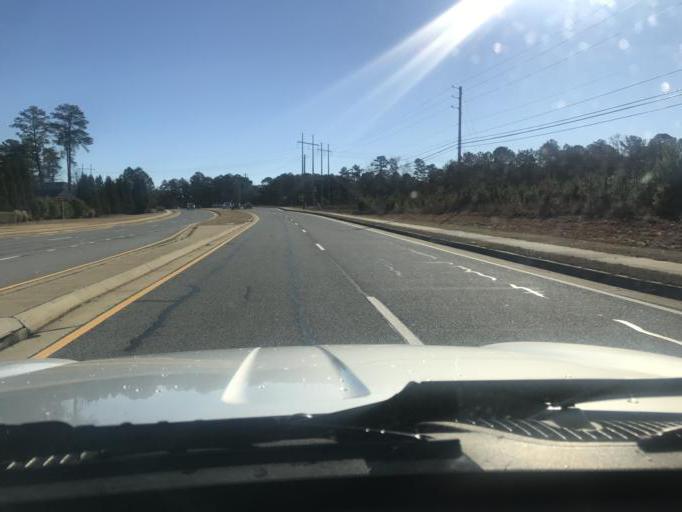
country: US
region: Georgia
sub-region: Gwinnett County
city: Lawrenceville
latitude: 33.9736
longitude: -84.0580
